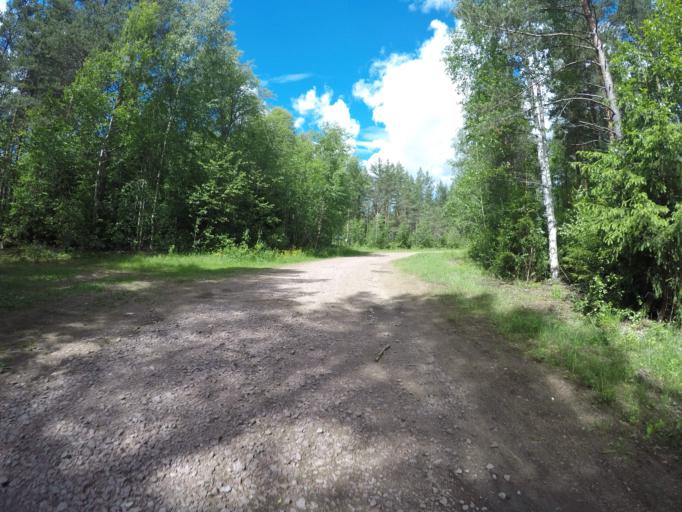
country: SE
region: Vaermland
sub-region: Filipstads Kommun
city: Lesjofors
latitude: 60.1367
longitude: 14.3019
